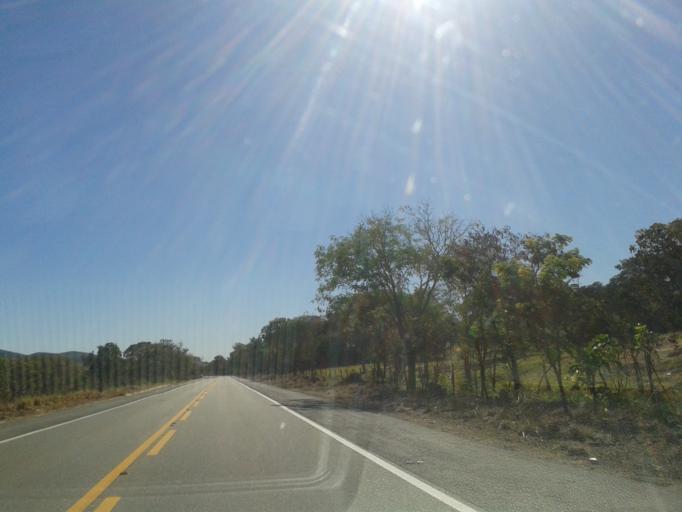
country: BR
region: Goias
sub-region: Goias
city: Goias
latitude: -15.8498
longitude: -50.0954
